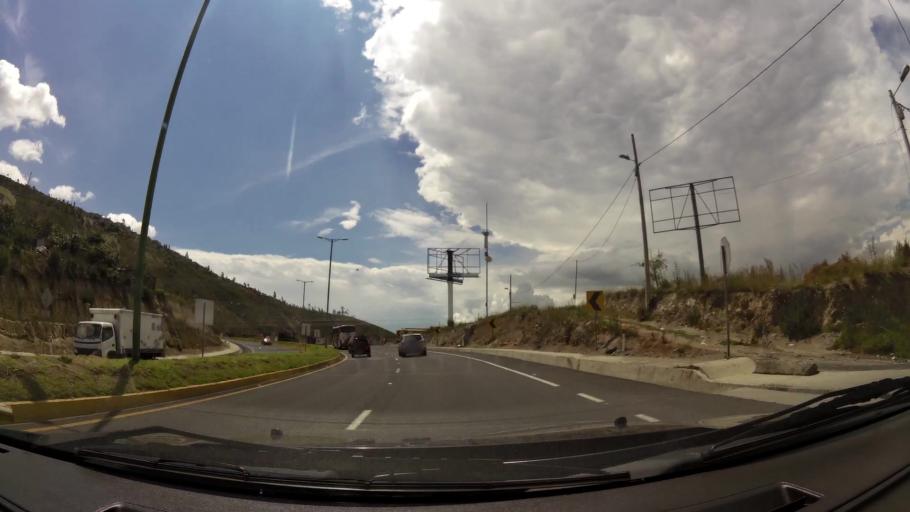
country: EC
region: Pichincha
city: Quito
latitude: -0.0943
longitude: -78.4089
